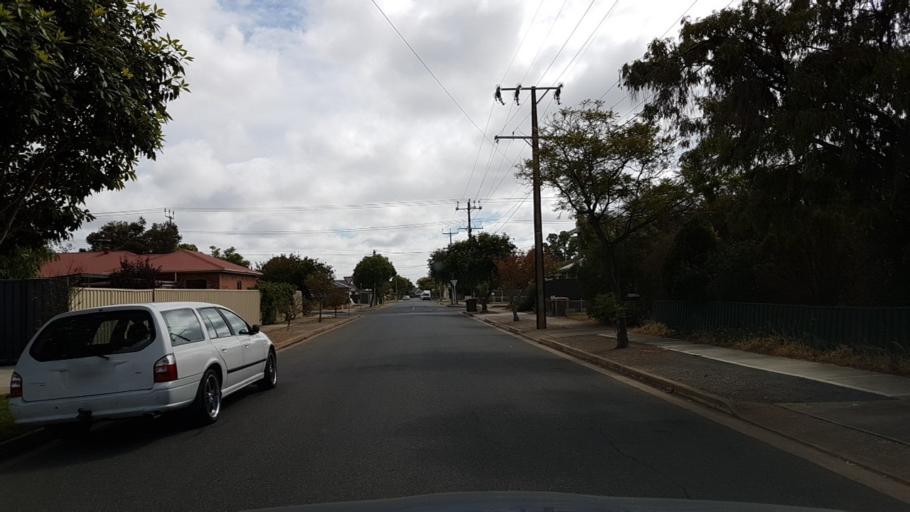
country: AU
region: South Australia
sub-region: Marion
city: South Plympton
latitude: -34.9781
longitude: 138.5515
